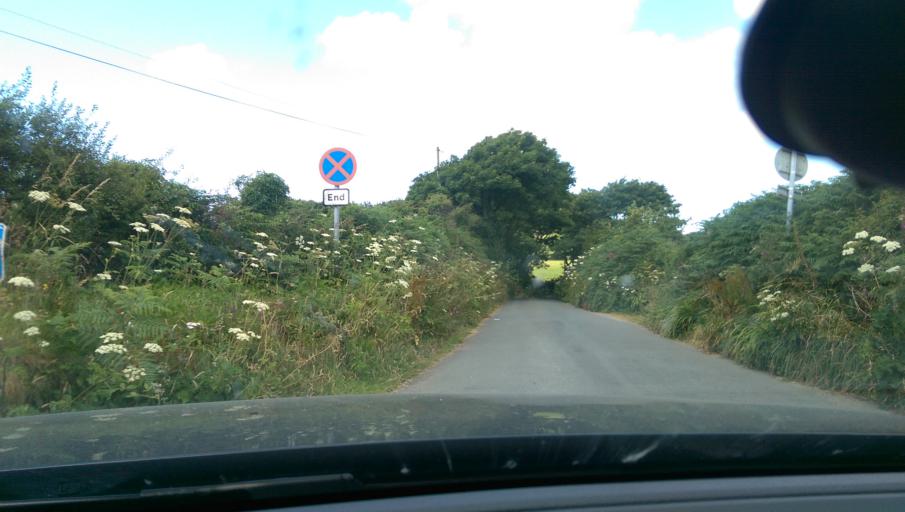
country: GB
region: England
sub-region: Cornwall
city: St. Buryan
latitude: 50.0958
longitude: -5.6151
